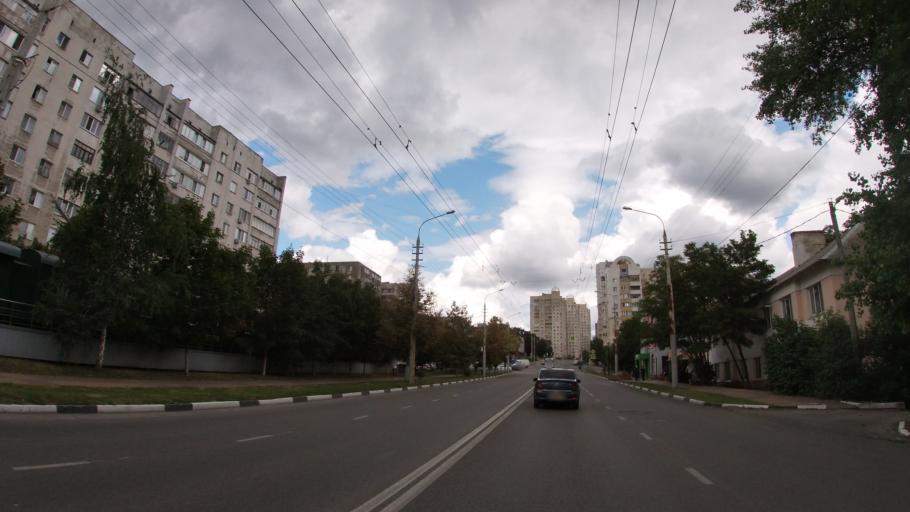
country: RU
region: Belgorod
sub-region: Belgorodskiy Rayon
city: Belgorod
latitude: 50.5972
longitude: 36.6065
